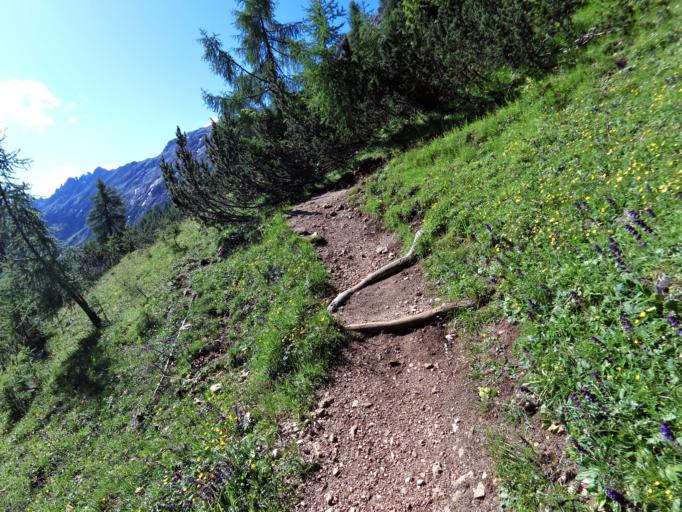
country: IT
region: Trentino-Alto Adige
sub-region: Bolzano
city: Siusi
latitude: 46.5124
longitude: 11.5954
